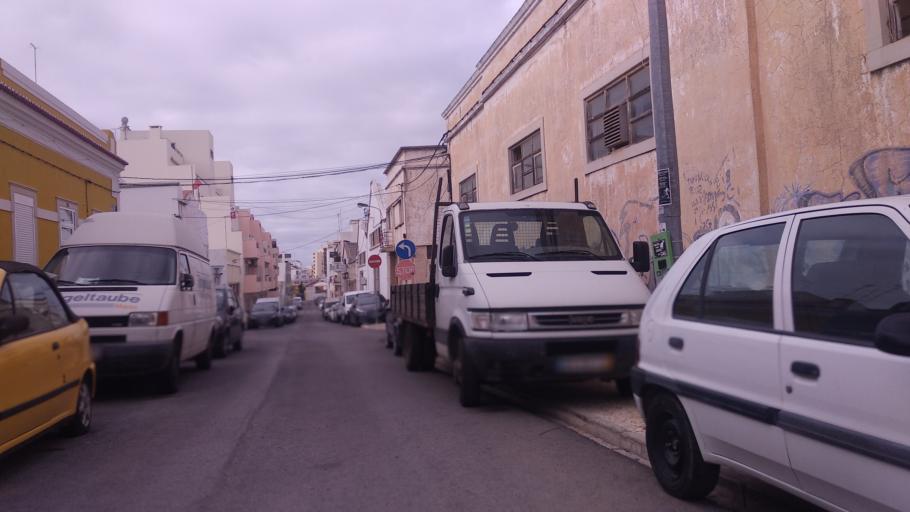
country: PT
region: Faro
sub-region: Faro
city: Faro
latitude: 37.0228
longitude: -7.9340
